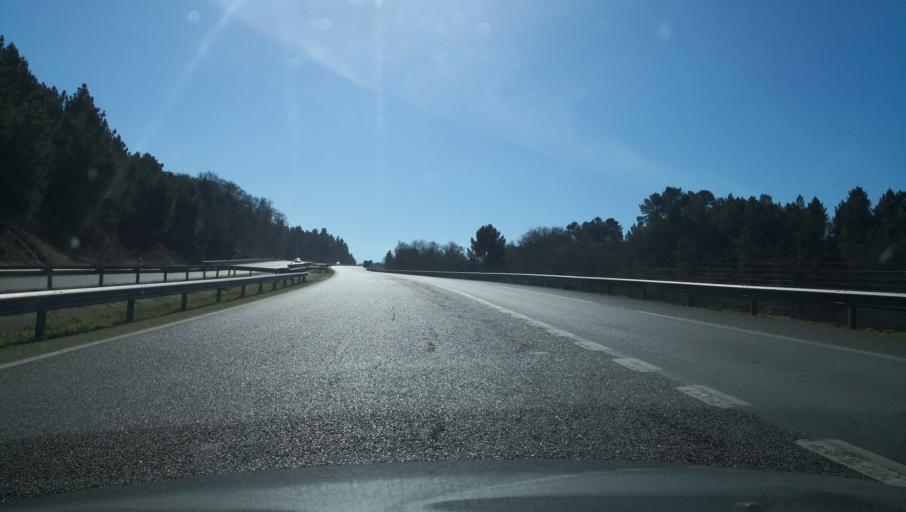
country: ES
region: Galicia
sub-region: Provincia de Ourense
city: Taboadela
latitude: 42.2757
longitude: -7.8727
